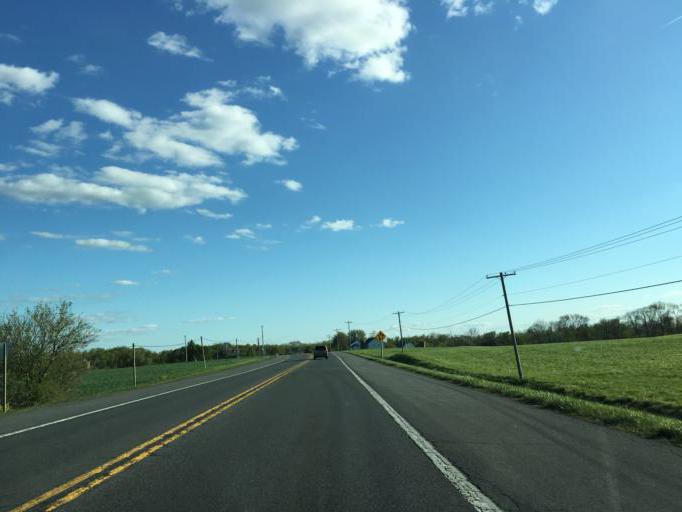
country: US
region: Maryland
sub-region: Frederick County
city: Walkersville
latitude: 39.4590
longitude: -77.3660
